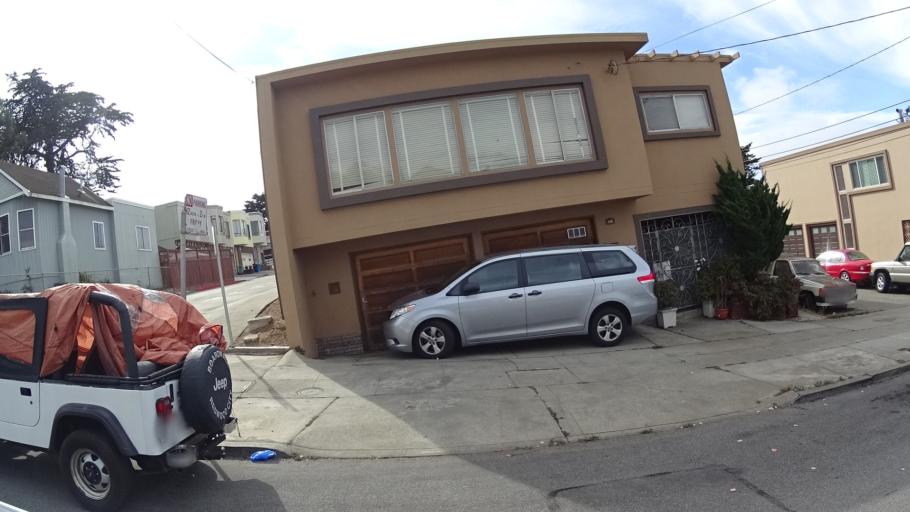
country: US
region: California
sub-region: San Mateo County
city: Daly City
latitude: 37.7087
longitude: -122.4424
